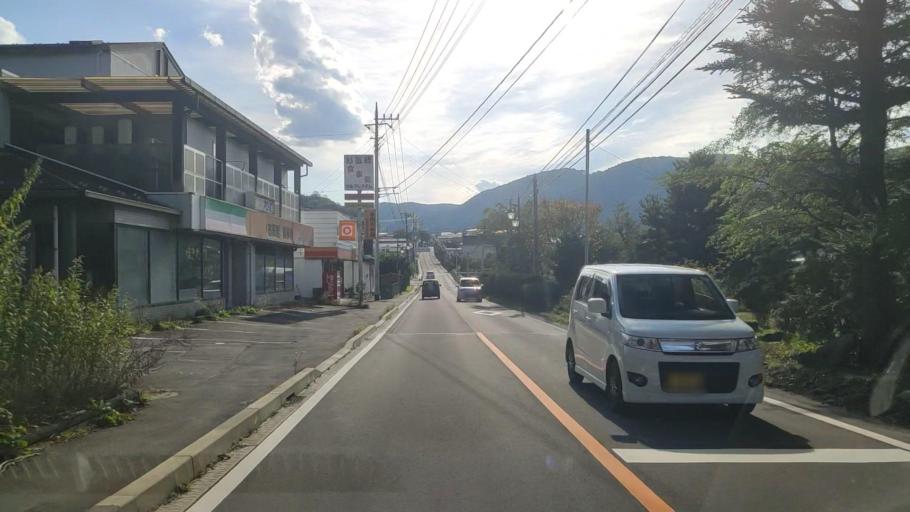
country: JP
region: Nagano
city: Komoro
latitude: 36.5059
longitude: 138.5098
